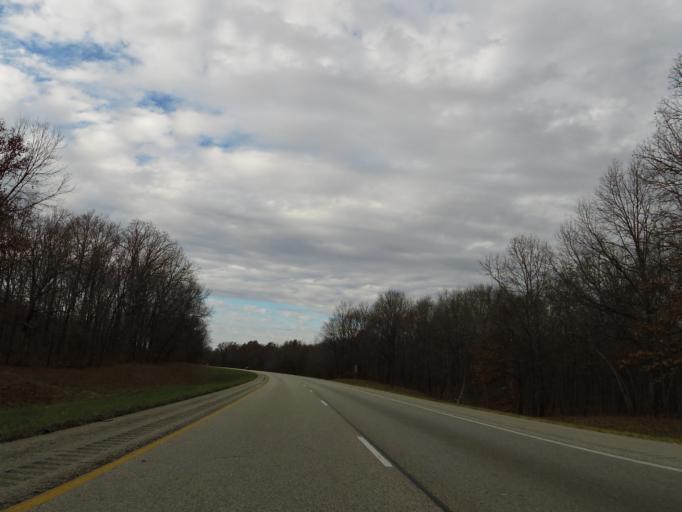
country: US
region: Illinois
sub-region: Washington County
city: Nashville
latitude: 38.3925
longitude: -89.3159
